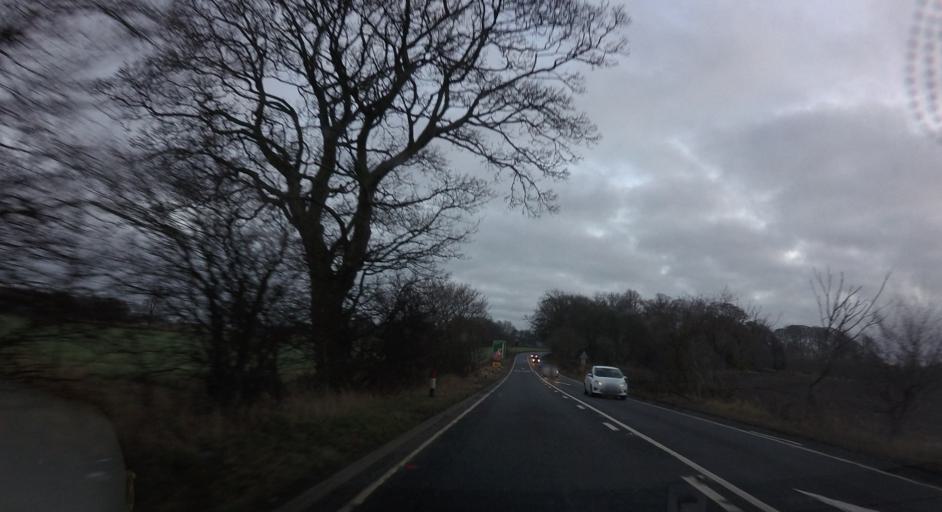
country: GB
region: Scotland
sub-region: Fife
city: Limekilns
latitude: 56.0438
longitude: -3.4737
